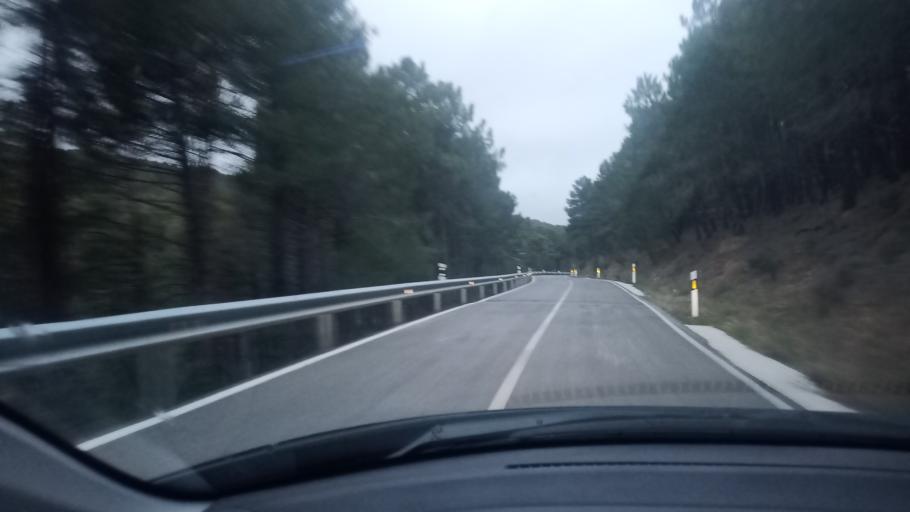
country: ES
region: Madrid
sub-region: Provincia de Madrid
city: Zarzalejo
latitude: 40.5534
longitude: -4.1851
